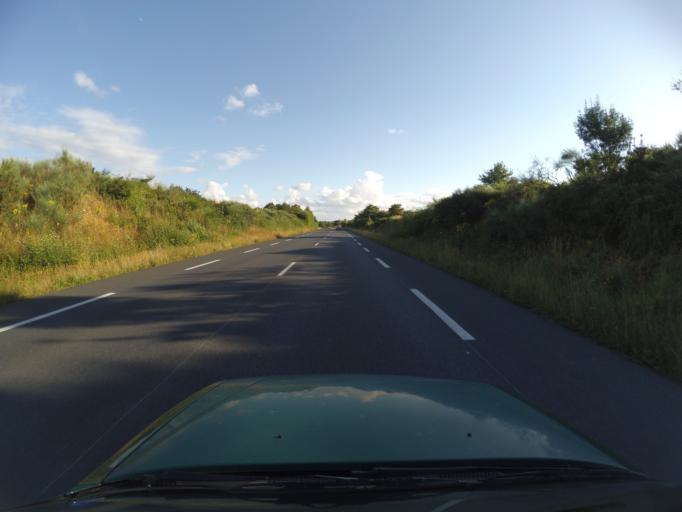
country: FR
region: Pays de la Loire
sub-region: Departement de la Vendee
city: Saint-Hilaire-de-Loulay
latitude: 47.0017
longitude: -1.3450
